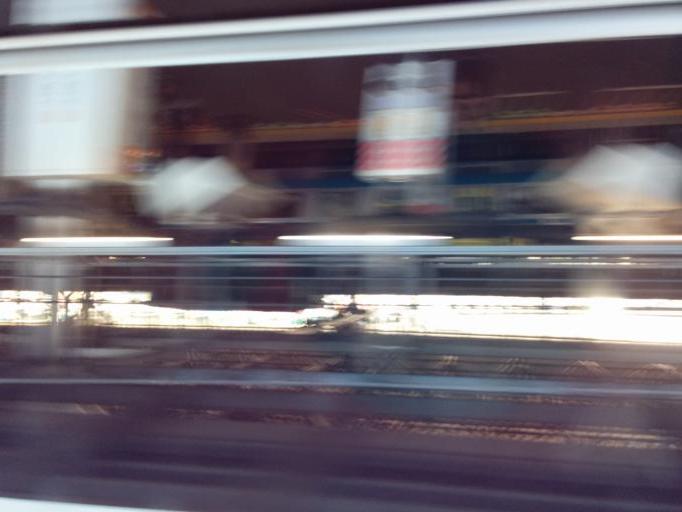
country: JP
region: Tokyo
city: Tokyo
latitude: 35.6661
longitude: 139.7586
